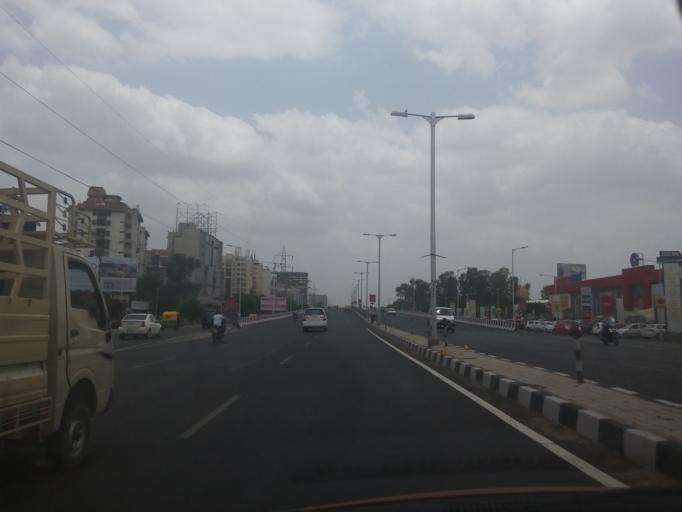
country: IN
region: Gujarat
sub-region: Ahmadabad
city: Sarkhej
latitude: 23.0316
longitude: 72.5088
